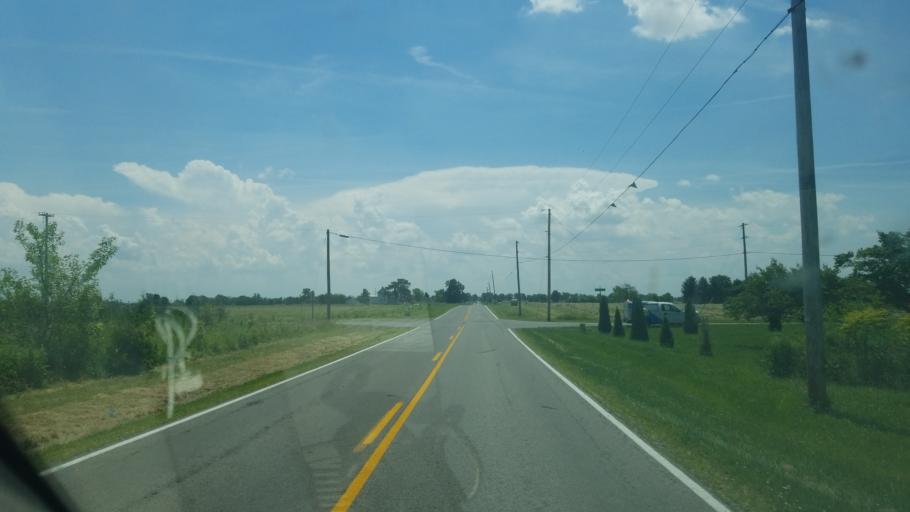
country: US
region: Ohio
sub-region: Hancock County
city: Arlington
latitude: 40.9505
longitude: -83.5942
